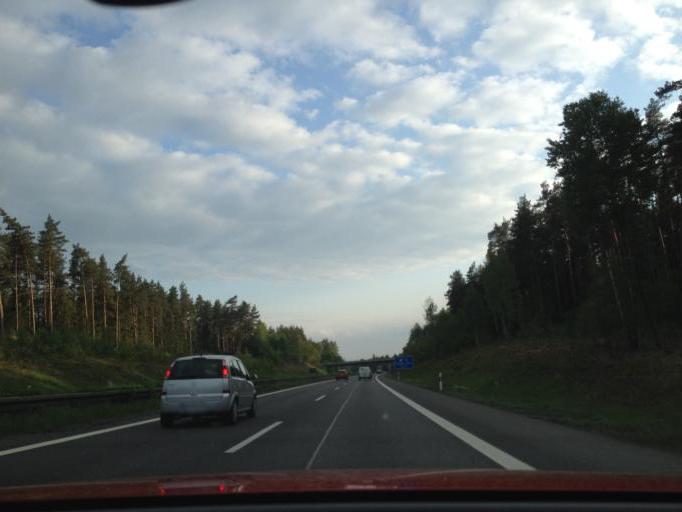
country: DE
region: Bavaria
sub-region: Upper Palatinate
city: Weiden
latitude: 49.7112
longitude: 12.1436
